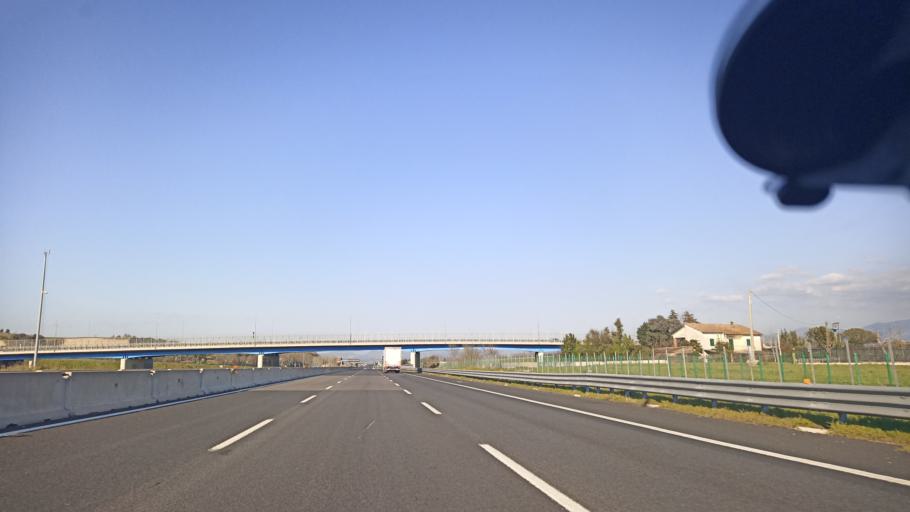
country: IT
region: Latium
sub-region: Citta metropolitana di Roma Capitale
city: Girardi-Bellavista-Terrazze
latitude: 42.0900
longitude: 12.5688
